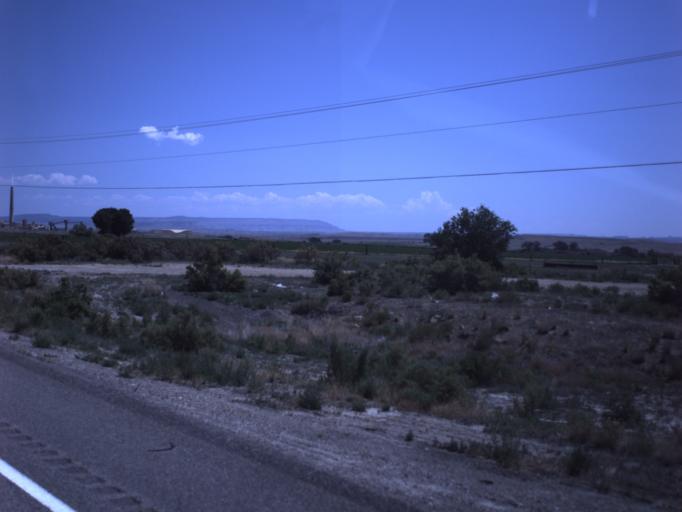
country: US
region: Utah
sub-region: Emery County
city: Orangeville
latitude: 39.1605
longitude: -111.0719
